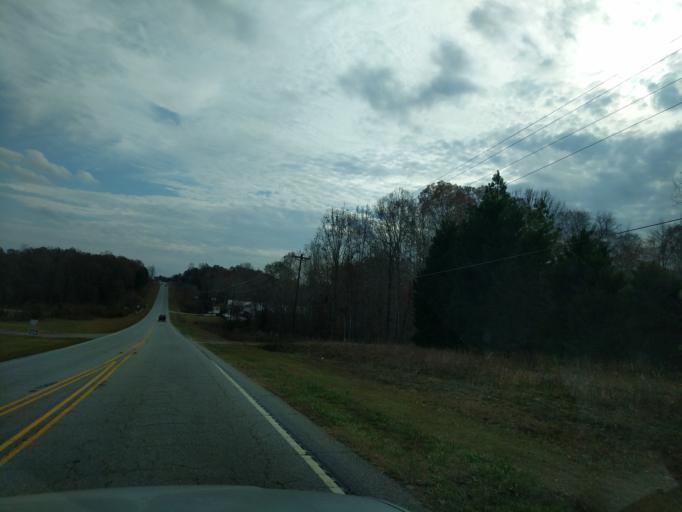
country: US
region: Georgia
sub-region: Franklin County
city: Gumlog
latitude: 34.5345
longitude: -83.0535
